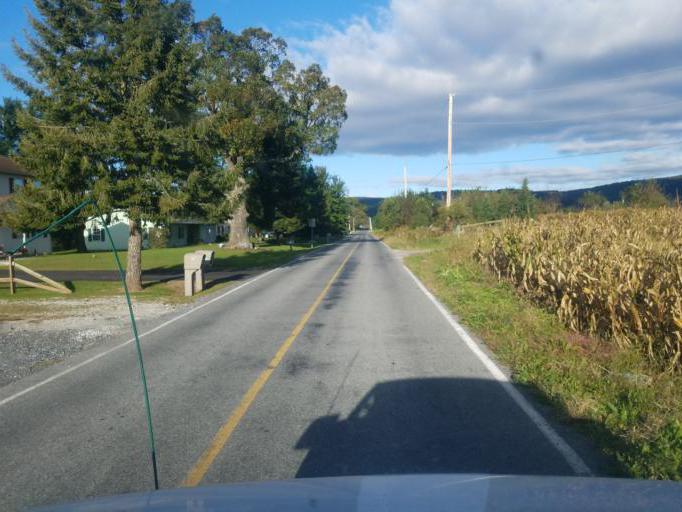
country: US
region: Pennsylvania
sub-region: Adams County
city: Biglerville
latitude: 39.8874
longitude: -77.3413
